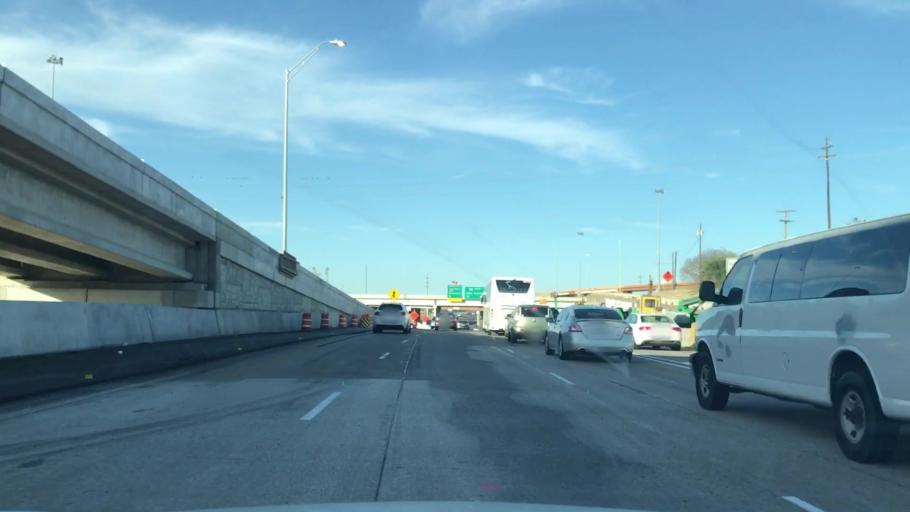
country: US
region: Texas
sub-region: Tarrant County
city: Fort Worth
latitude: 32.7518
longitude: -97.3207
